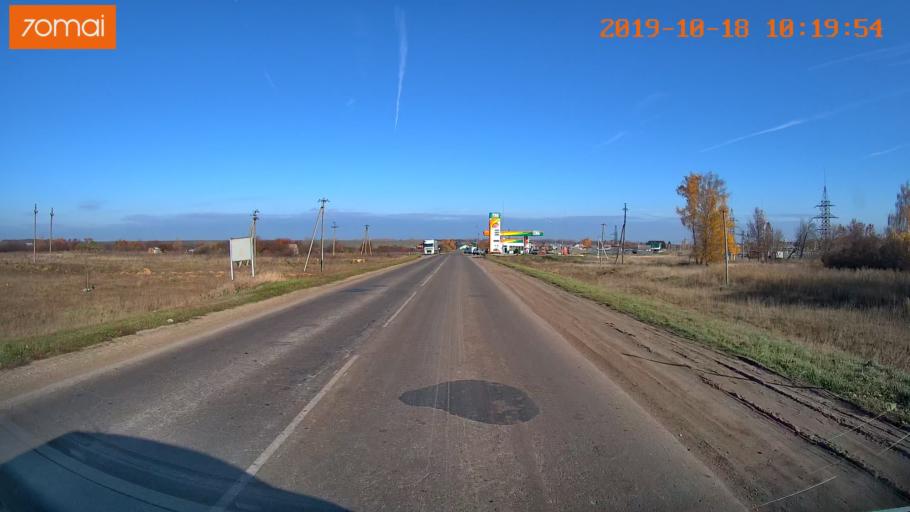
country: RU
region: Tula
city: Kurkino
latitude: 53.4251
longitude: 38.6448
